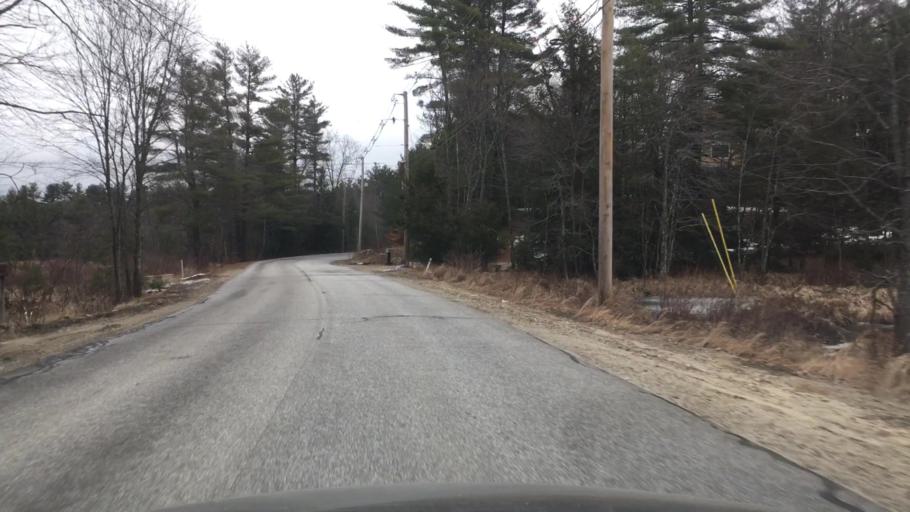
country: US
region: New Hampshire
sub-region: Hillsborough County
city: Goffstown
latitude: 42.9616
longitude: -71.6214
